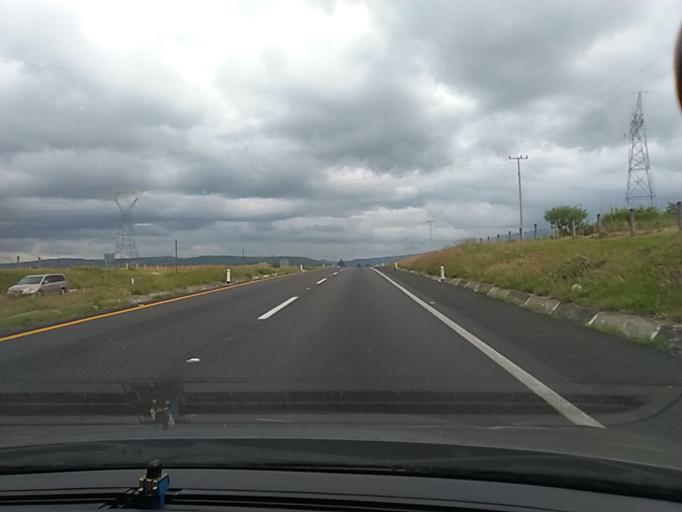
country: MX
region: Jalisco
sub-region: Zapotlanejo
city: La Mezquitera
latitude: 20.5983
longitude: -103.1150
